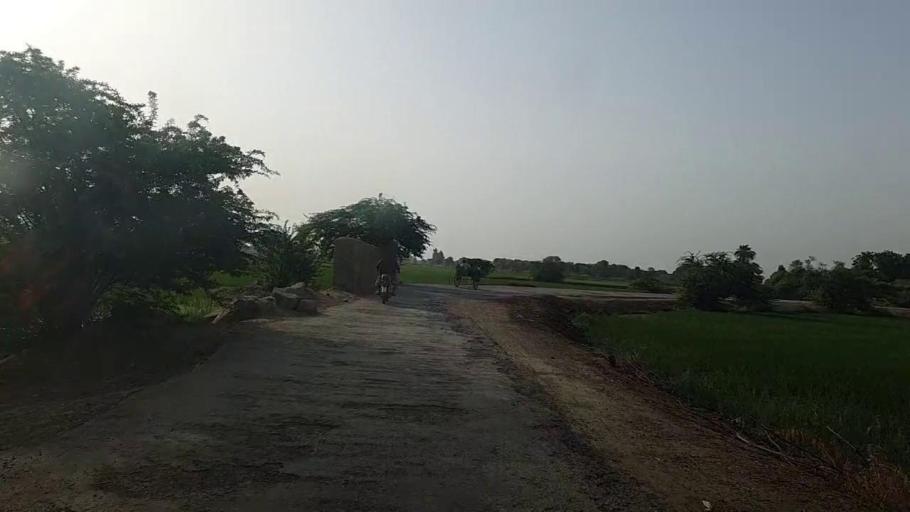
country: PK
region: Sindh
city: Mehar
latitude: 27.1339
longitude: 67.7909
